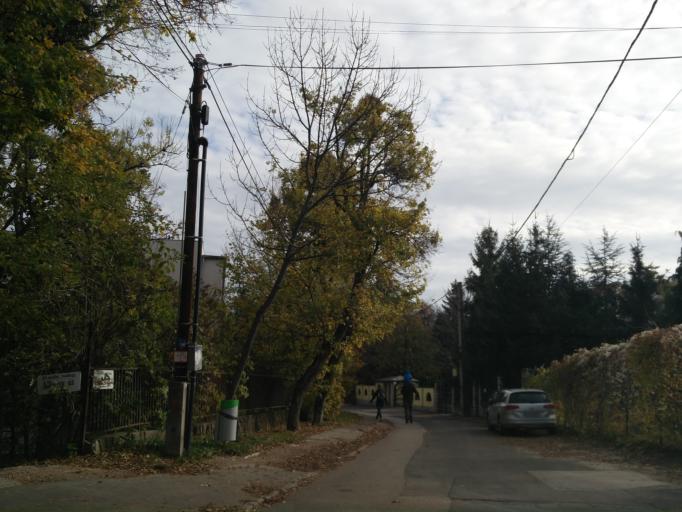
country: HU
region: Budapest
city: Budapest XII. keruelet
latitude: 47.5039
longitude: 18.9756
